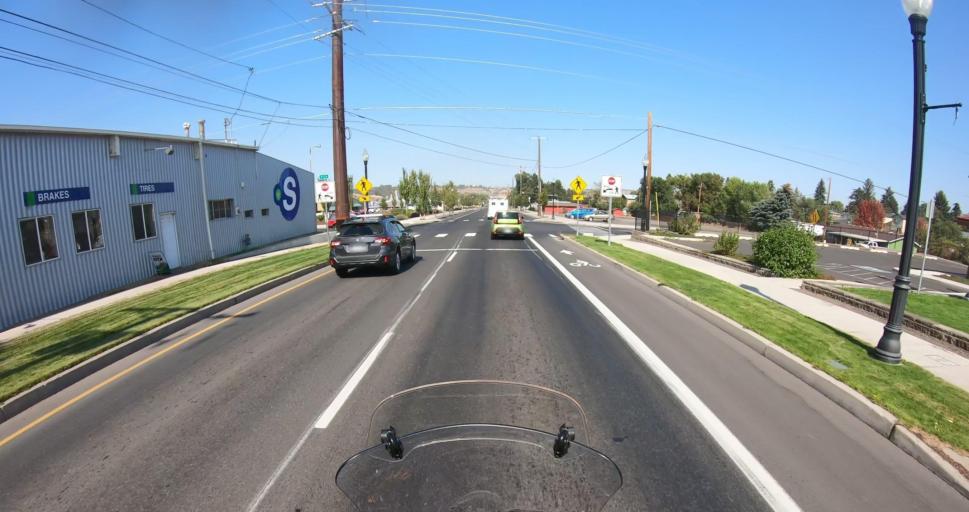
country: US
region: Oregon
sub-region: Jefferson County
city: Madras
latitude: 44.6247
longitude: -121.1294
